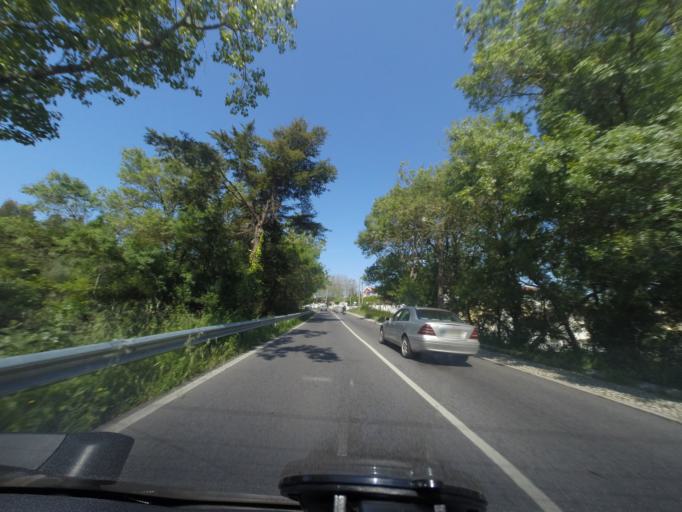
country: PT
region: Lisbon
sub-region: Sintra
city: Sintra
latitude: 38.8096
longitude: -9.3739
